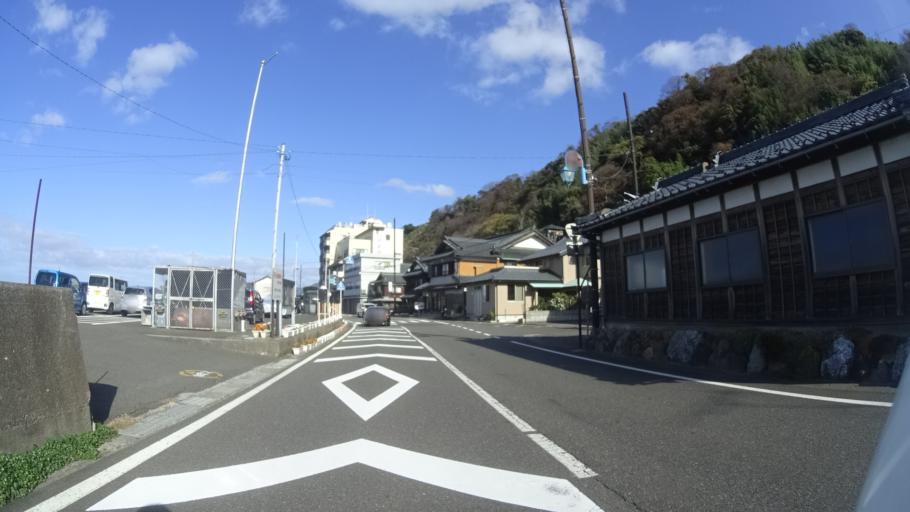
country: JP
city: Asahi
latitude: 35.9090
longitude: 135.9971
